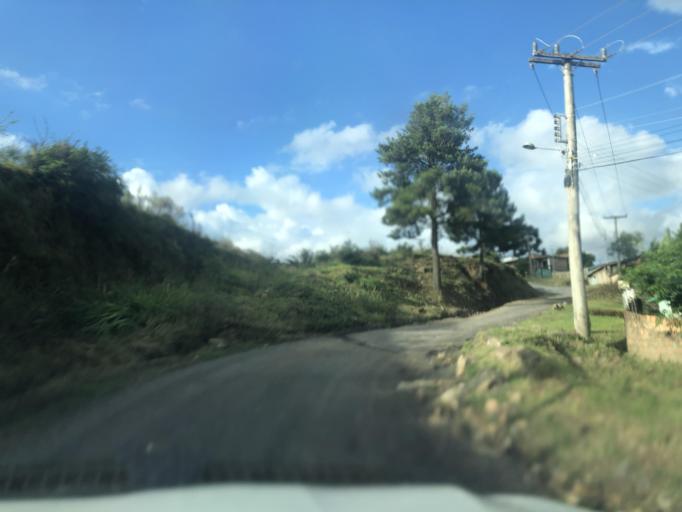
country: BR
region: Santa Catarina
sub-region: Lages
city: Lages
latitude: -27.7936
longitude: -50.3172
